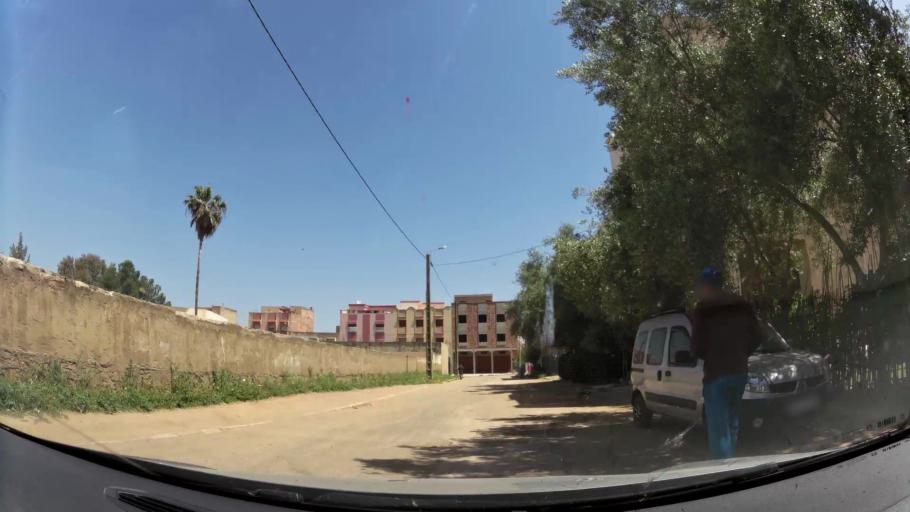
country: MA
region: Rabat-Sale-Zemmour-Zaer
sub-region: Khemisset
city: Khemisset
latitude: 33.8104
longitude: -6.0731
